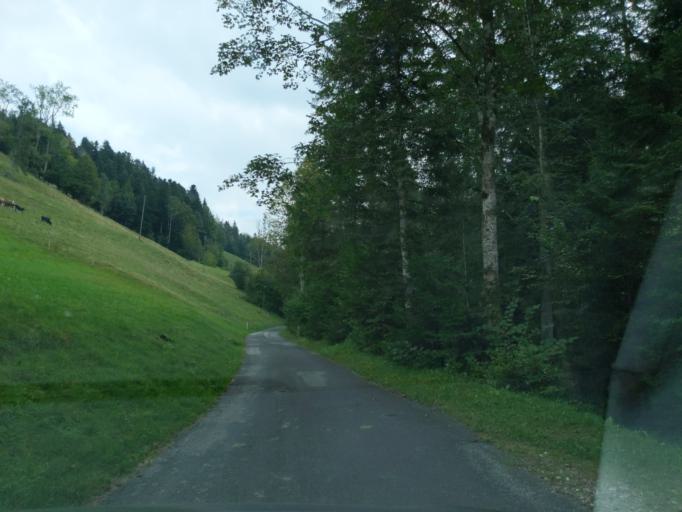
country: CH
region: Bern
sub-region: Oberaargau
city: Wyssachen
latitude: 47.0406
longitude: 7.8243
